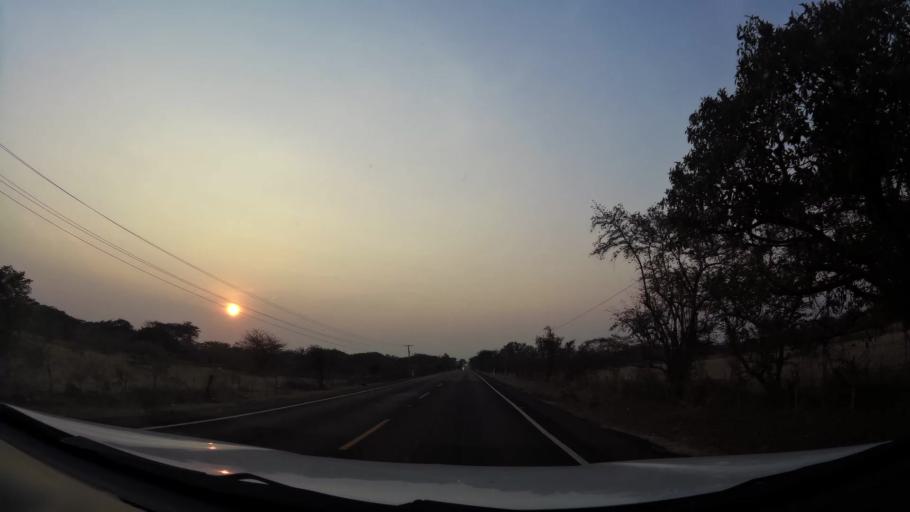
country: NI
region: Leon
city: La Paz Centro
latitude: 12.3181
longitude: -86.7918
